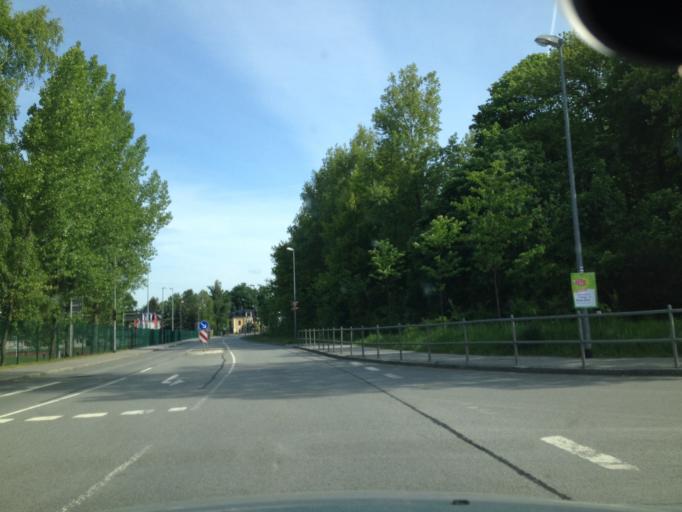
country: DE
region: Saxony
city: Annaberg-Buchholz
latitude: 50.5771
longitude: 13.0145
